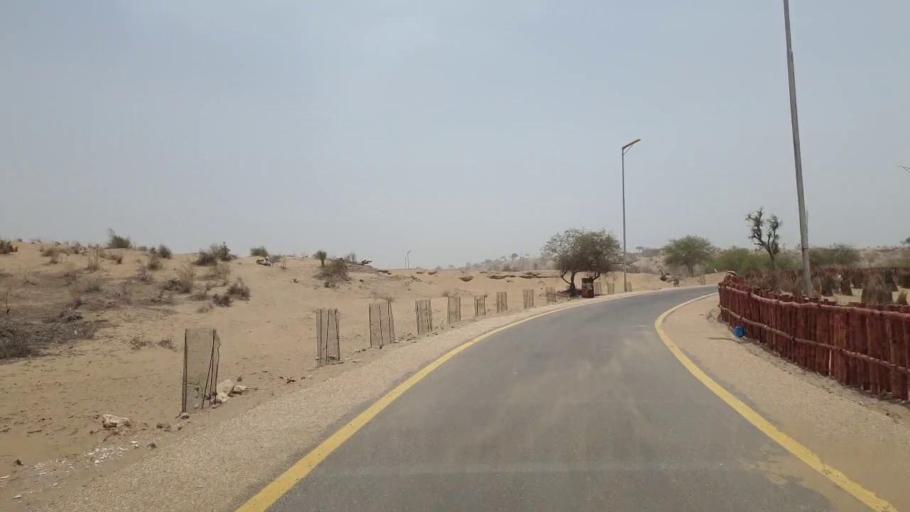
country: PK
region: Sindh
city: Islamkot
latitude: 24.7248
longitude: 70.3245
